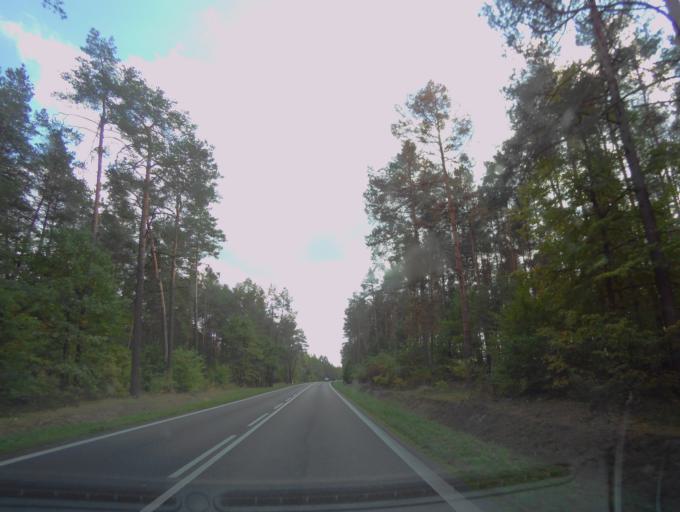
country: PL
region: Lublin Voivodeship
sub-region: Powiat bilgorajski
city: Frampol
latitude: 50.6039
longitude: 22.6773
